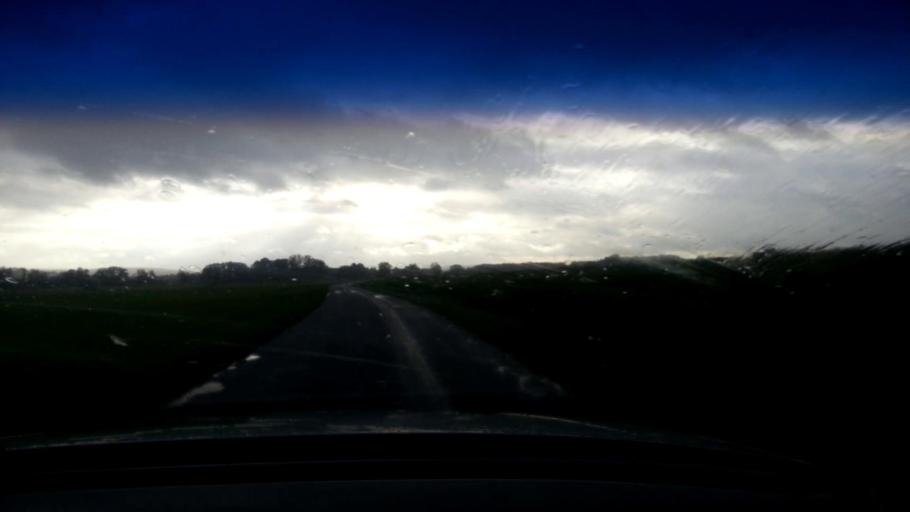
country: DE
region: Bavaria
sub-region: Upper Franconia
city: Burgebrach
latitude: 49.8289
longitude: 10.7198
